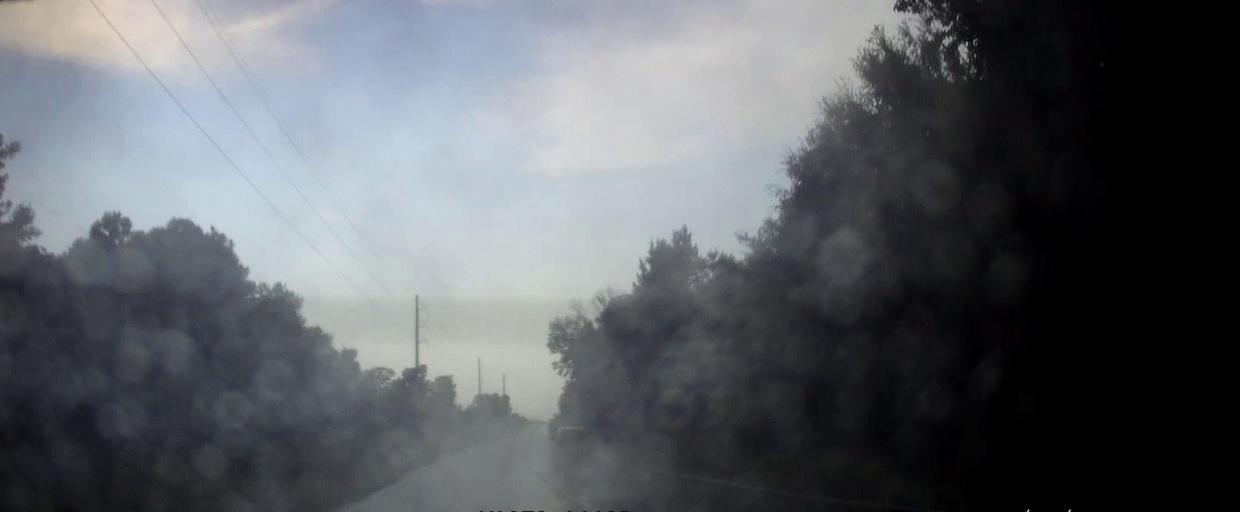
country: US
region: Georgia
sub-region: Twiggs County
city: Jeffersonville
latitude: 32.5741
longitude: -83.1998
